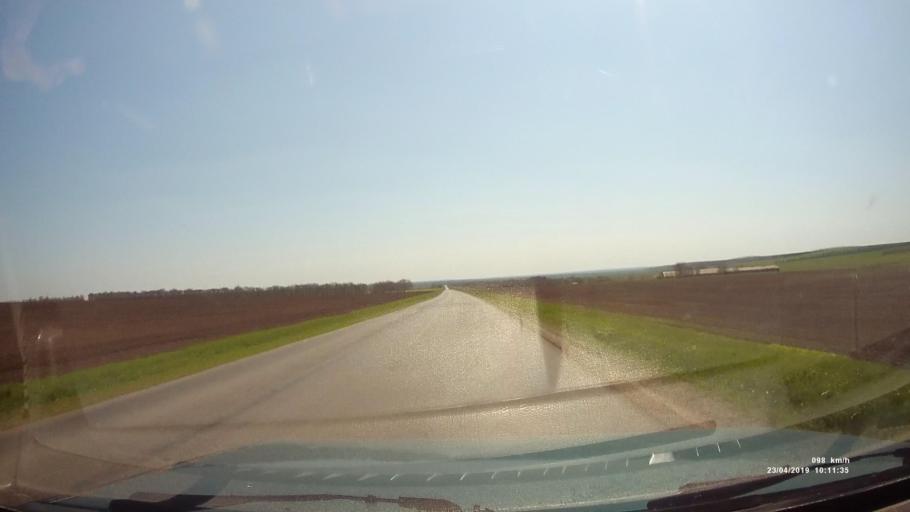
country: RU
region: Rostov
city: Sovetskoye
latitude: 46.6937
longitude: 42.3224
